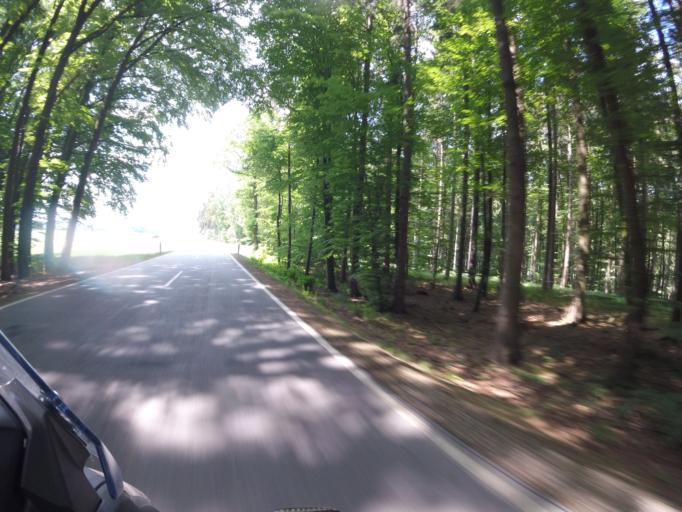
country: DE
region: Bavaria
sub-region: Lower Bavaria
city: Wildenberg
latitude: 48.7314
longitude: 11.9238
